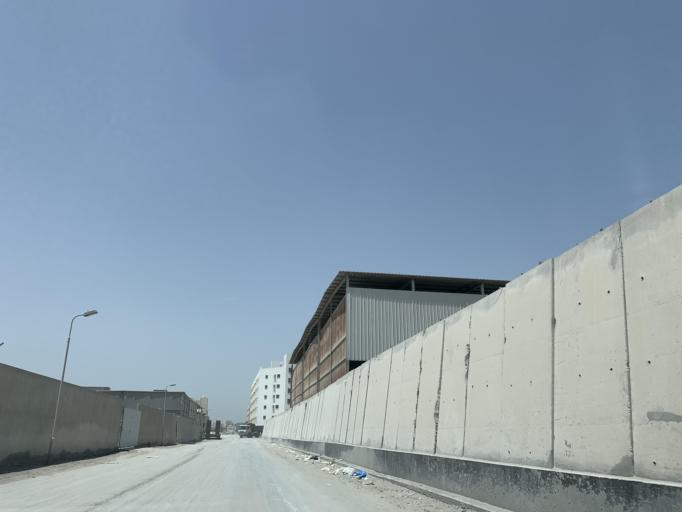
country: BH
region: Northern
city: Sitrah
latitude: 26.1464
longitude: 50.5984
